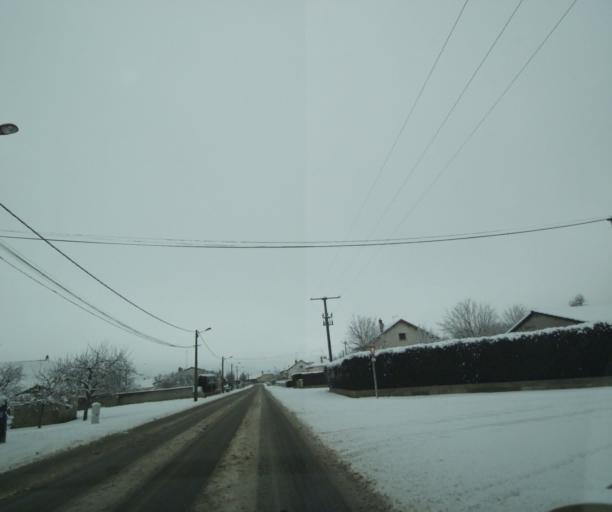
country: FR
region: Champagne-Ardenne
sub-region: Departement de la Haute-Marne
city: Wassy
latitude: 48.5295
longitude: 4.9276
